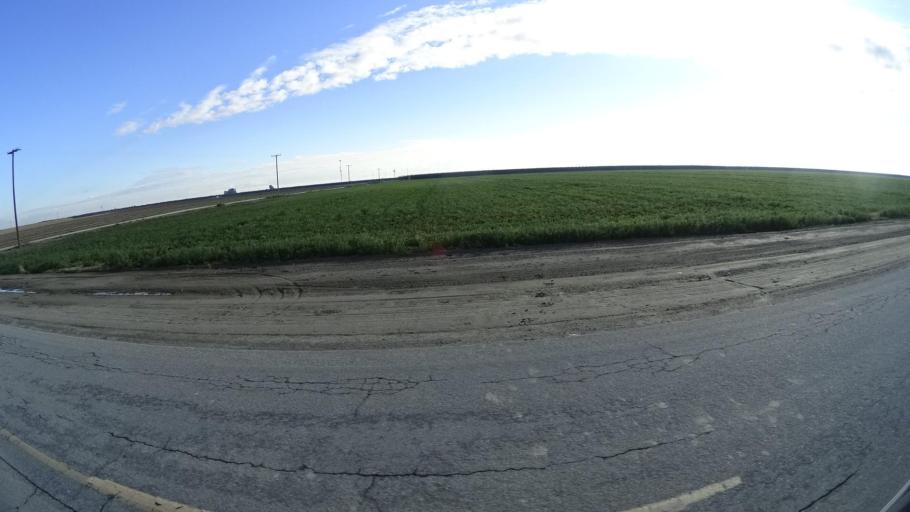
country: US
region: California
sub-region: Kern County
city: Delano
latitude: 35.7500
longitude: -119.3299
